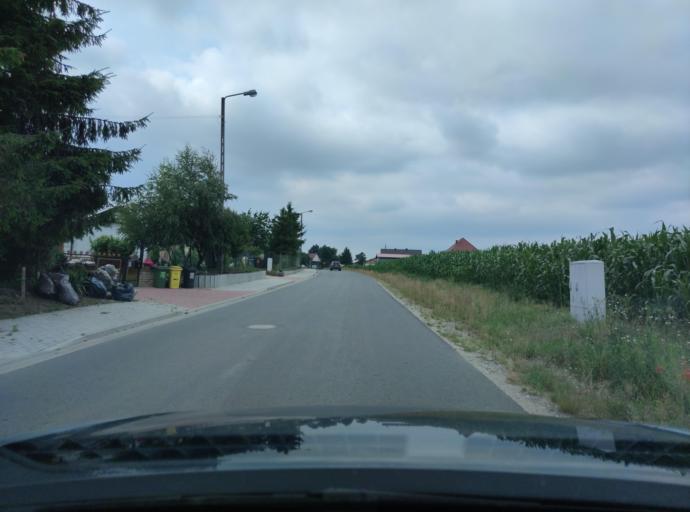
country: PL
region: Lower Silesian Voivodeship
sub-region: Powiat wroclawski
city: Tyniec Maly
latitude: 50.9962
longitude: 16.9135
